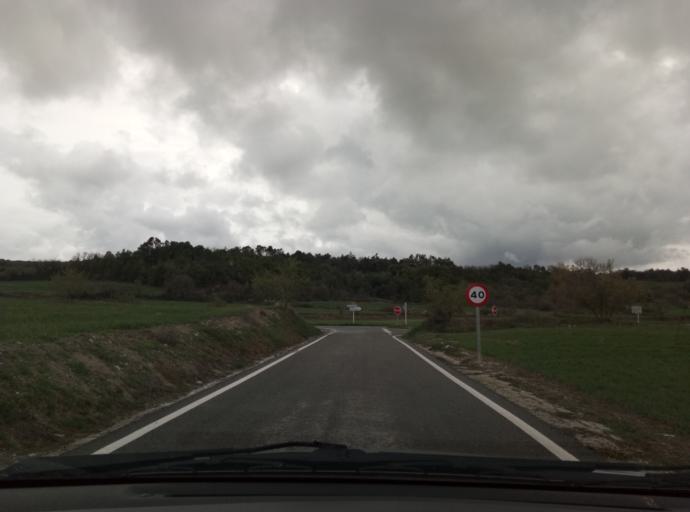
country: ES
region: Catalonia
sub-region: Provincia de Tarragona
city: Santa Coloma de Queralt
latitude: 41.5429
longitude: 1.3619
